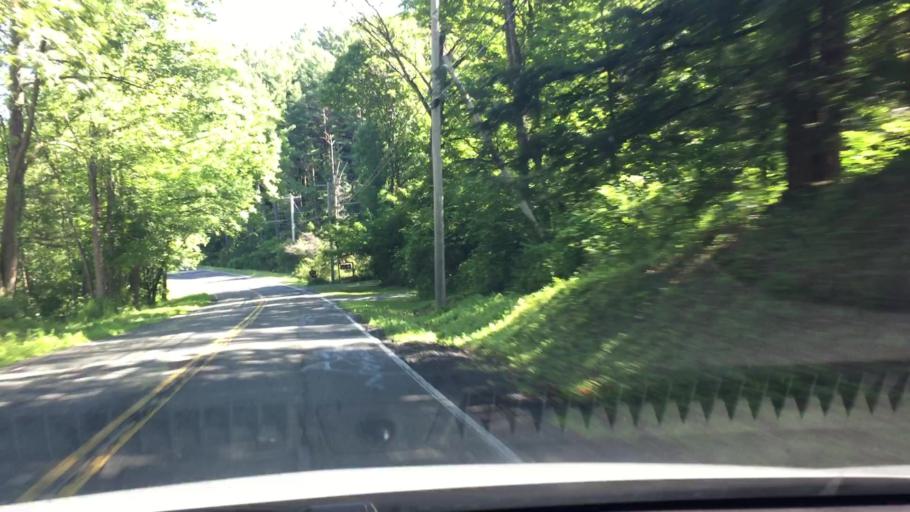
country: US
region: Massachusetts
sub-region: Berkshire County
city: West Stockbridge
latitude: 42.3086
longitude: -73.3699
